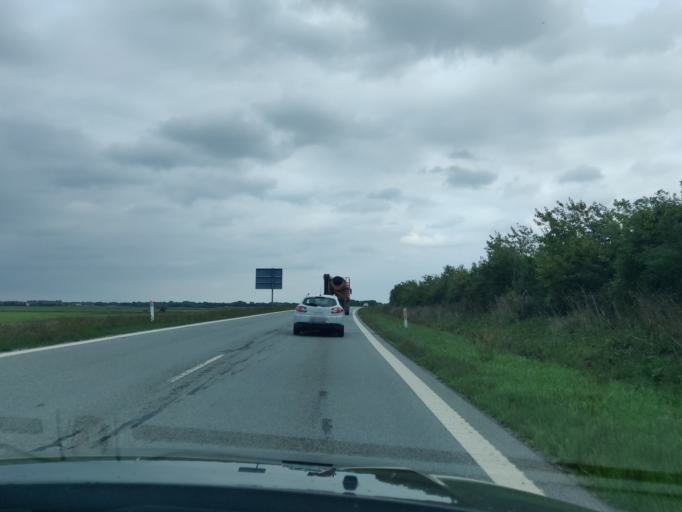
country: DK
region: North Denmark
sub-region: Alborg Kommune
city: Frejlev
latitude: 57.0113
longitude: 9.7426
